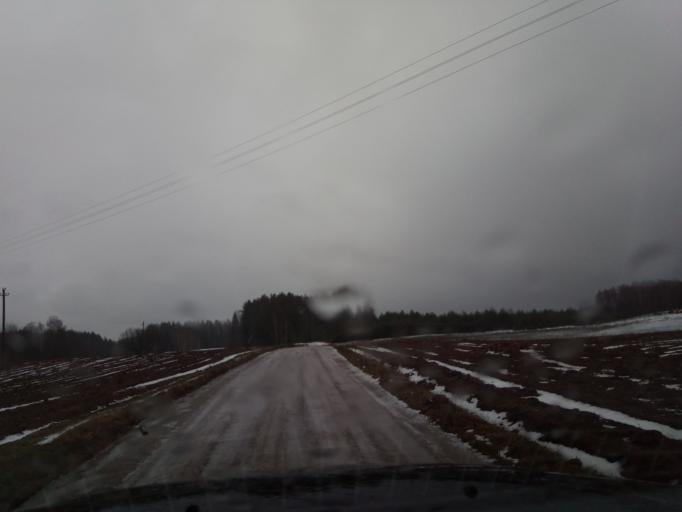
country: LT
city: Svencioneliai
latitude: 55.3426
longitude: 25.8429
